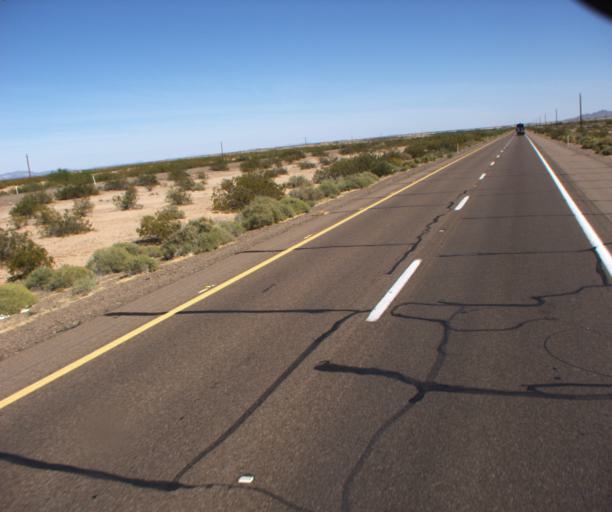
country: US
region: Arizona
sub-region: Yuma County
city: Wellton
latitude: 32.7436
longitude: -113.6795
